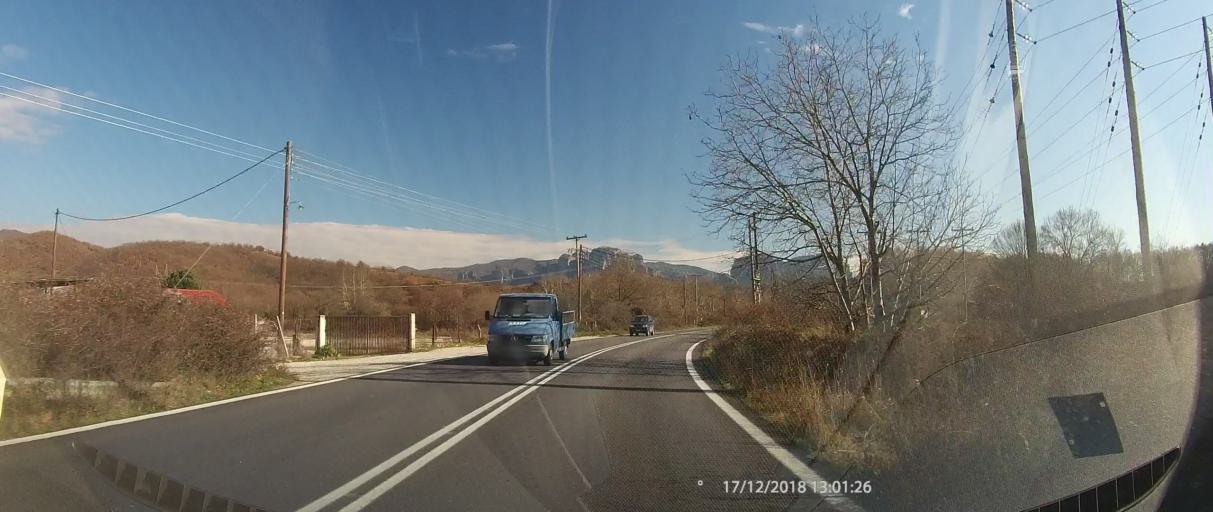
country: GR
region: Thessaly
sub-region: Trikala
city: Kastraki
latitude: 39.7326
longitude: 21.5823
